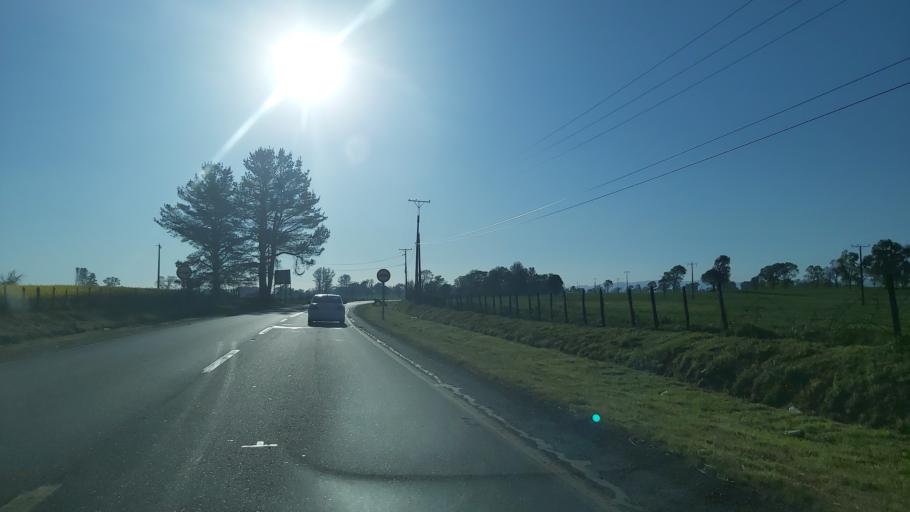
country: CL
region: Araucania
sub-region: Provincia de Malleco
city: Victoria
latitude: -38.2536
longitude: -72.2878
